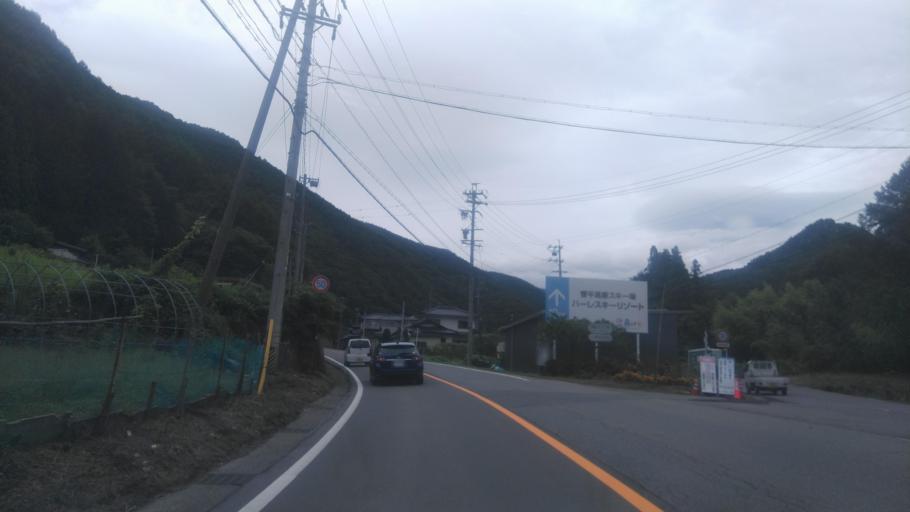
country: JP
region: Nagano
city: Ueda
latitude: 36.4723
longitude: 138.3445
